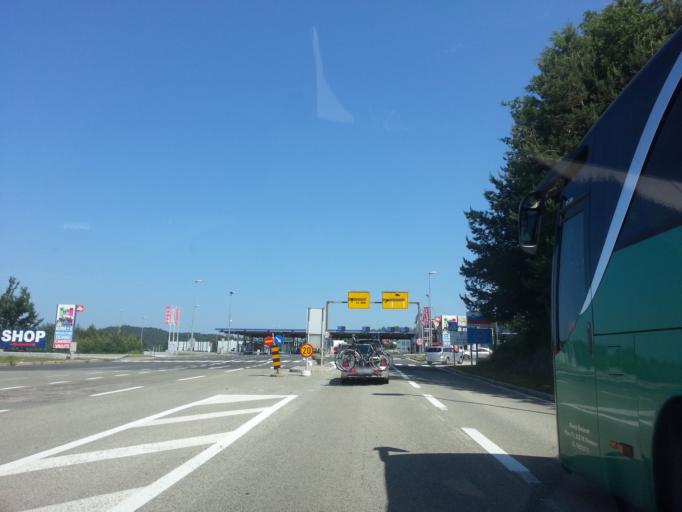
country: SI
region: Ilirska Bistrica
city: Ilirska Bistrica
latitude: 45.4892
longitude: 14.2782
